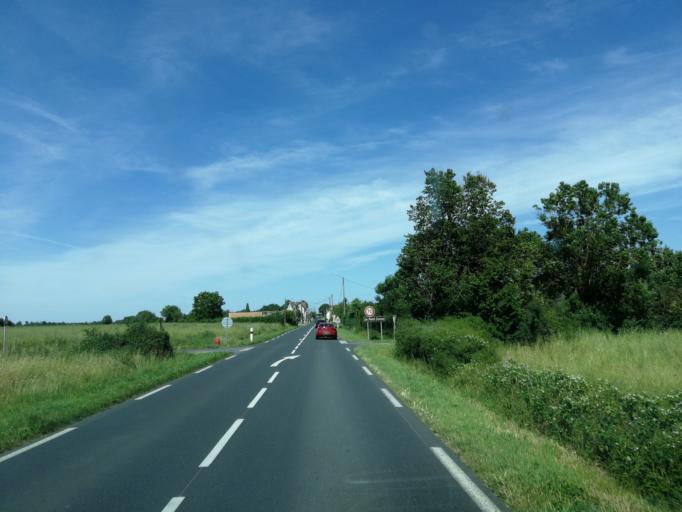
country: FR
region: Poitou-Charentes
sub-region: Departement des Deux-Sevres
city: Saint-Jean-de-Thouars
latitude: 46.9454
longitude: -0.2328
